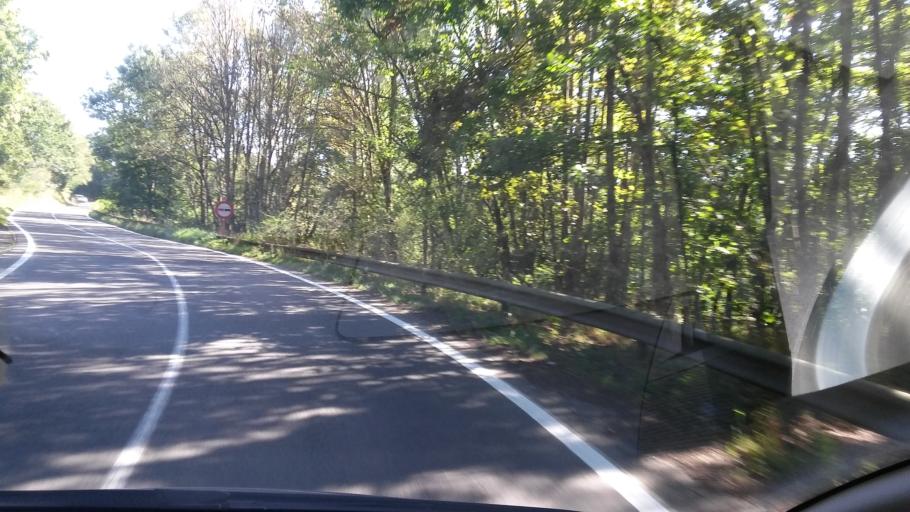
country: BE
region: Wallonia
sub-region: Province du Luxembourg
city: Neufchateau
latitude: 49.8355
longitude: 5.4207
